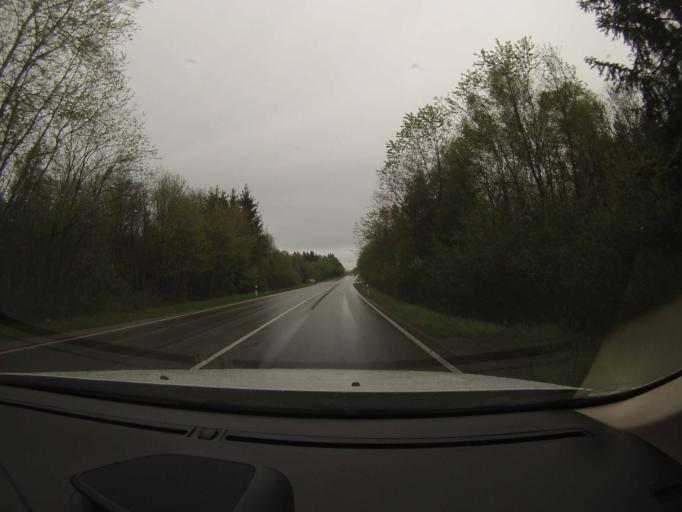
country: DE
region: Bavaria
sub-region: Upper Bavaria
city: Taufkirchen
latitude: 48.0214
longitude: 11.6358
